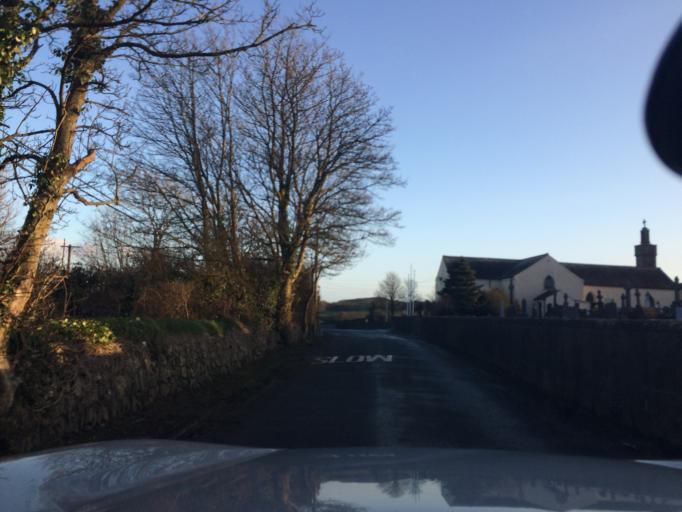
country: IE
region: Munster
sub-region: Waterford
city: Tra Mhor
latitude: 52.2256
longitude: -7.1817
